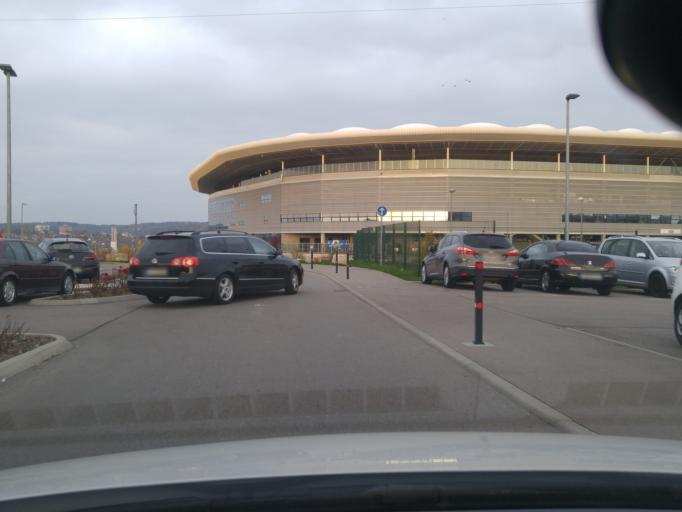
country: DE
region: Baden-Wuerttemberg
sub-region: Karlsruhe Region
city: Sinsheim
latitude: 49.2368
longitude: 8.8850
